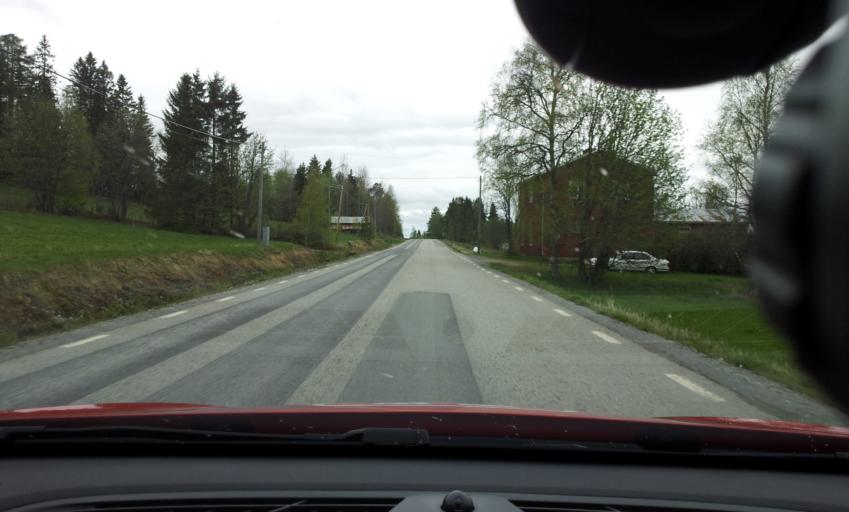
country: SE
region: Jaemtland
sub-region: Bergs Kommun
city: Hoverberg
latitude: 62.7770
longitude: 14.5171
